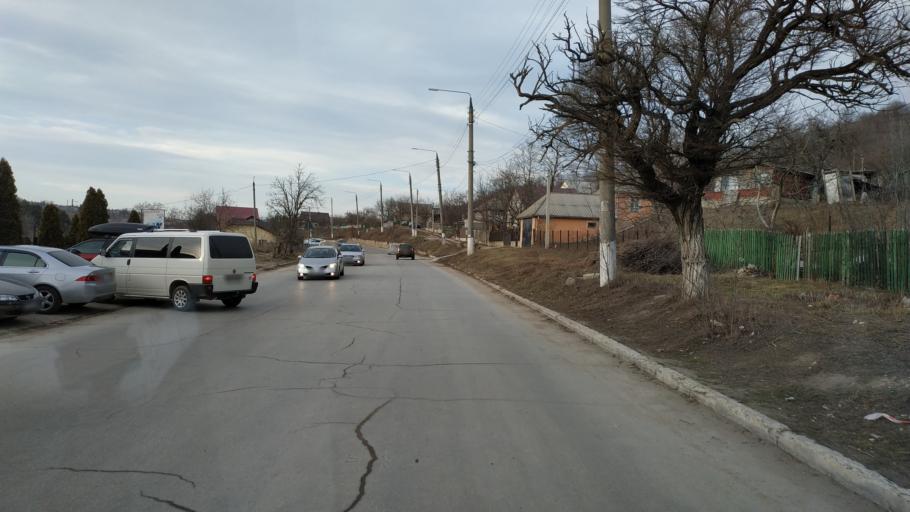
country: MD
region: Nisporeni
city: Nisporeni
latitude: 47.0873
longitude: 28.1823
